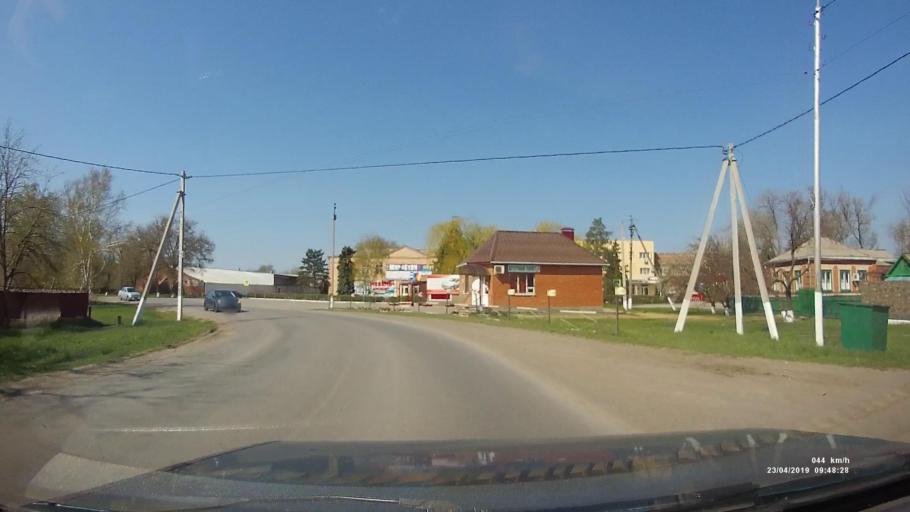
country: RU
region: Rostov
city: Orlovskiy
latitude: 46.8706
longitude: 42.0348
